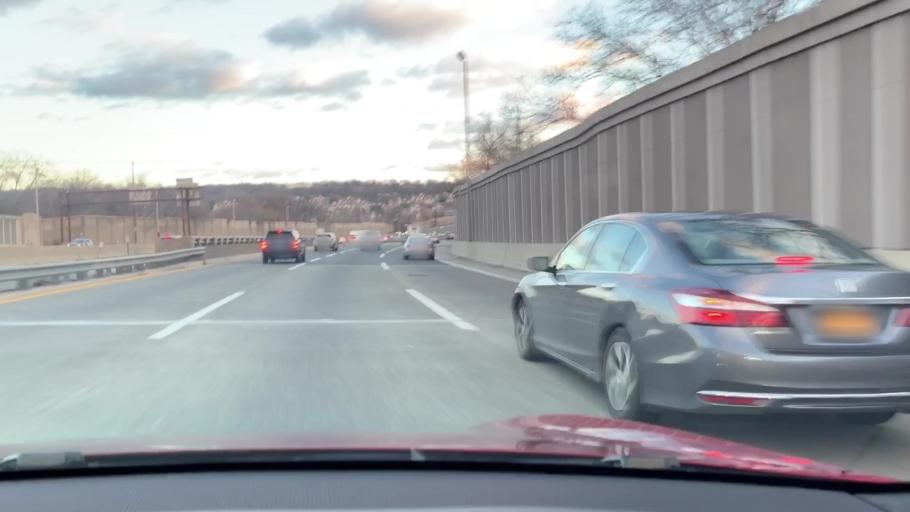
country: US
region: New Jersey
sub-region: Bergen County
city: Leonia
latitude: 40.8753
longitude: -73.9858
